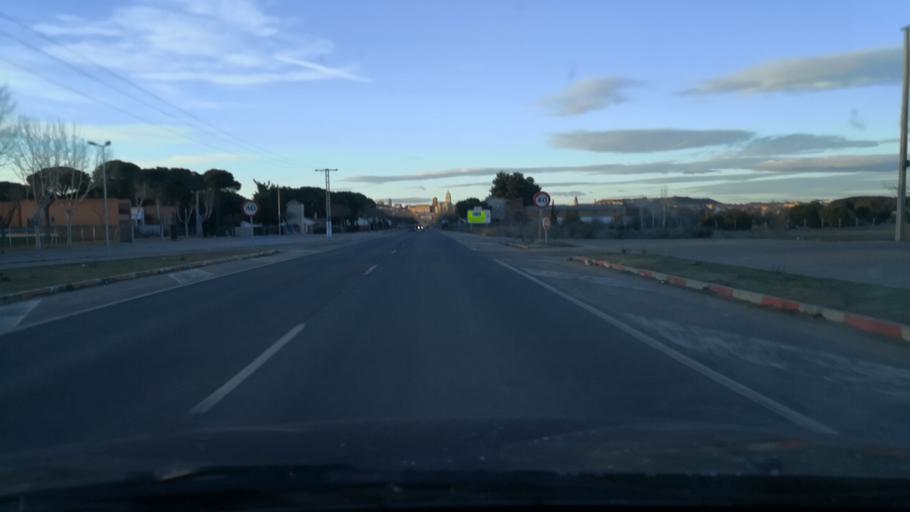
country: ES
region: Castille and Leon
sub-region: Provincia de Valladolid
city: Tordesillas
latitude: 41.4884
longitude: -4.9961
